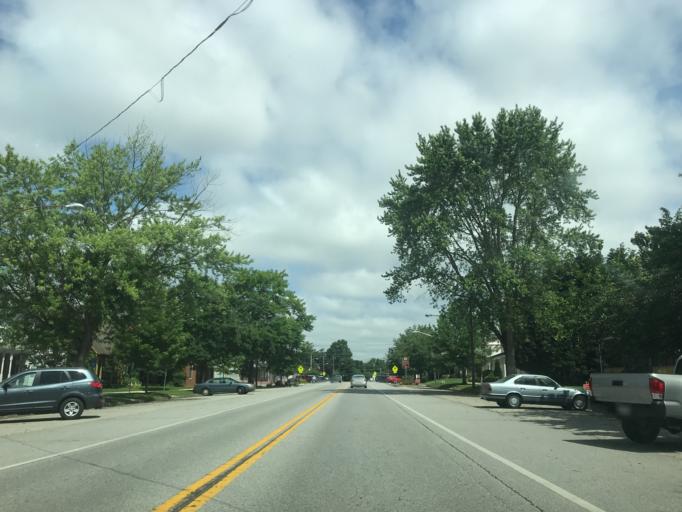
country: US
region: Maryland
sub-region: Caroline County
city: Ridgely
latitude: 38.9458
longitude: -75.8832
